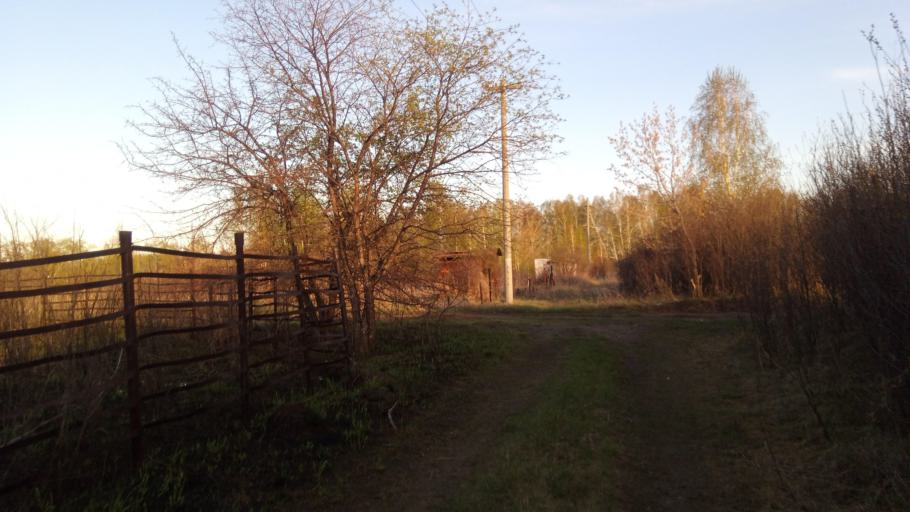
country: RU
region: Chelyabinsk
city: Timiryazevskiy
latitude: 54.9889
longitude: 60.8482
